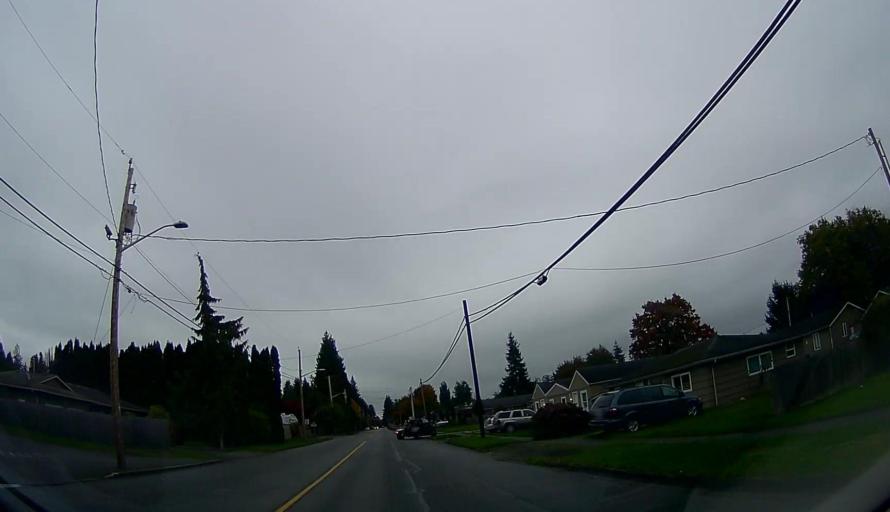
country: US
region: Washington
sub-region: Skagit County
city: Sedro-Woolley
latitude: 48.5033
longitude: -122.2246
